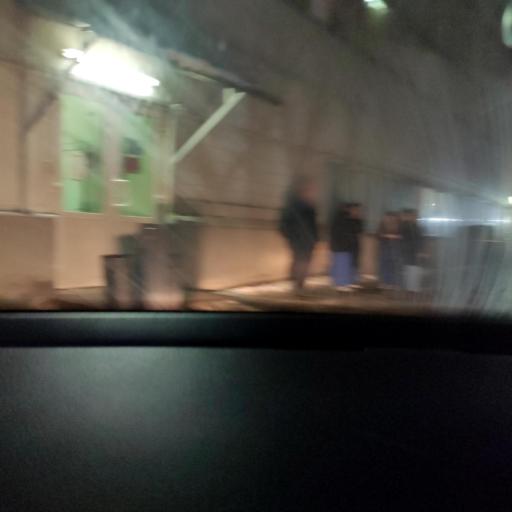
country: RU
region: Moscow
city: Mar'ina Roshcha
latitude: 55.8074
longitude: 37.6045
